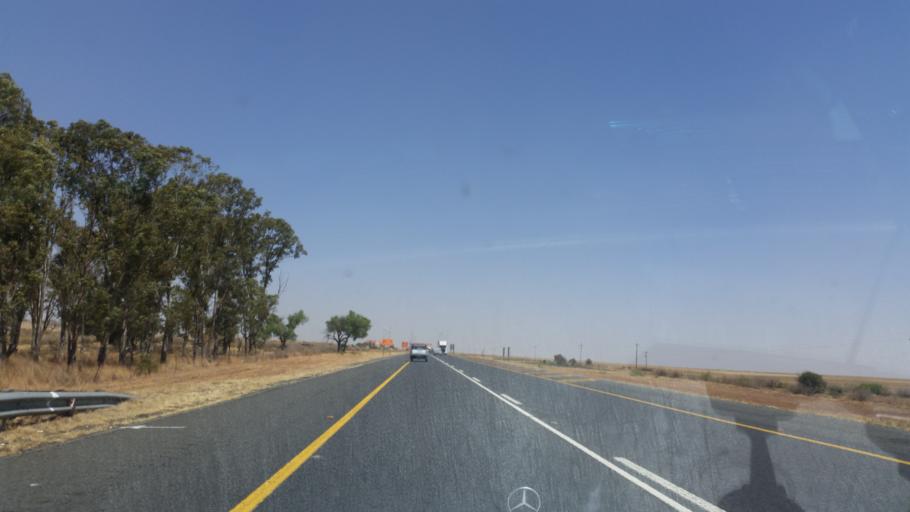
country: ZA
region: Orange Free State
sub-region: Lejweleputswa District Municipality
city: Brandfort
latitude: -28.7926
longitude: 26.6986
